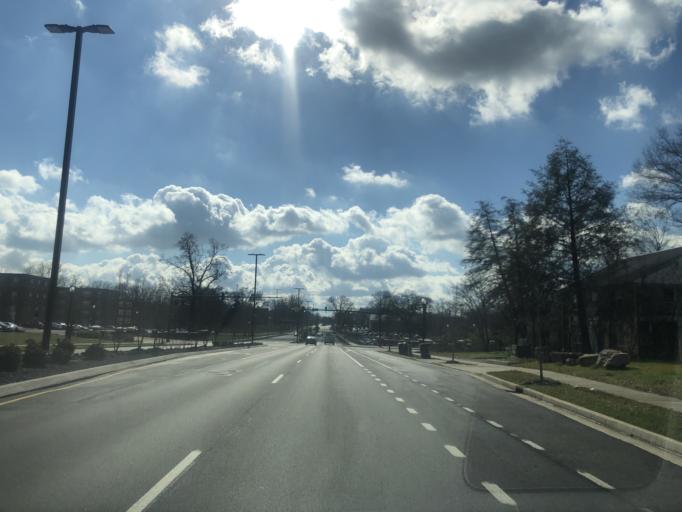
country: US
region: Tennessee
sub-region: Rutherford County
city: Murfreesboro
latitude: 35.8490
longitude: -86.3714
